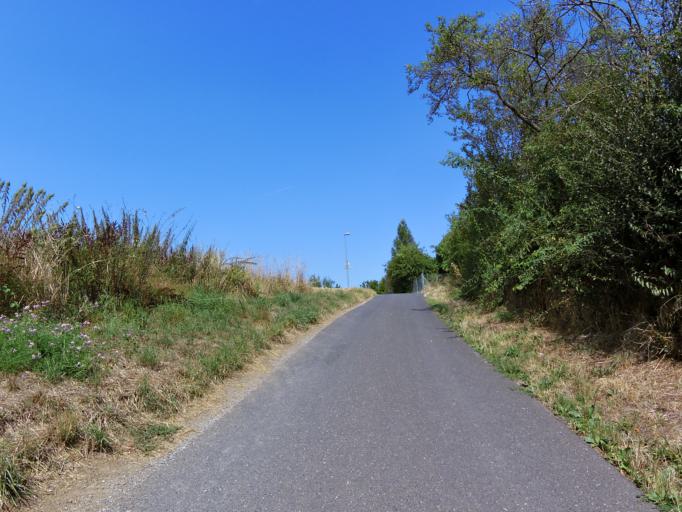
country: DE
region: Bavaria
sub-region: Regierungsbezirk Unterfranken
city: Zell am Main
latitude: 49.8177
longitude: 9.8649
